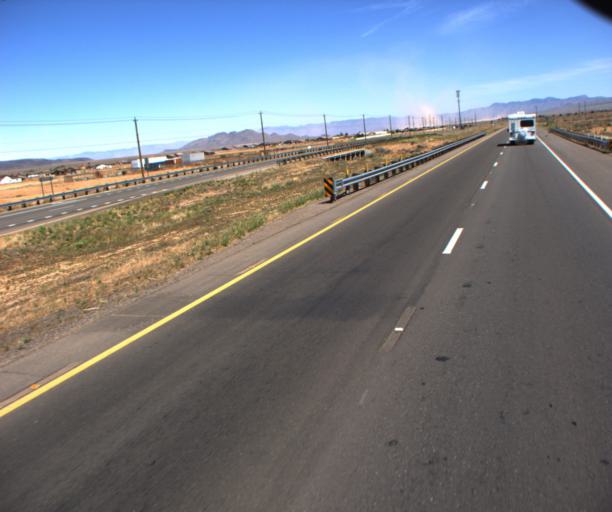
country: US
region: Arizona
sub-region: Mohave County
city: New Kingman-Butler
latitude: 35.2583
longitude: -113.9710
